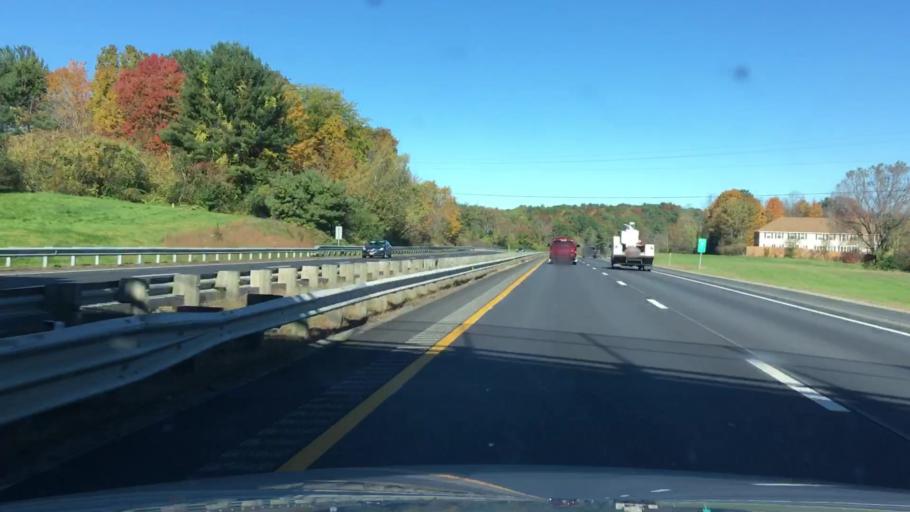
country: US
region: New Hampshire
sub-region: Strafford County
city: Dover
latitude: 43.2002
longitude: -70.8969
